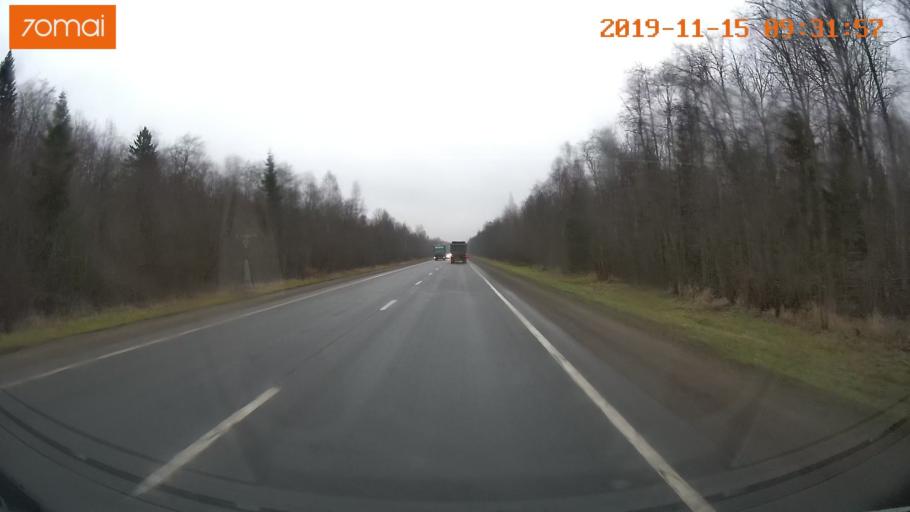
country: RU
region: Vologda
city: Sheksna
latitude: 59.2735
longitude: 38.3230
